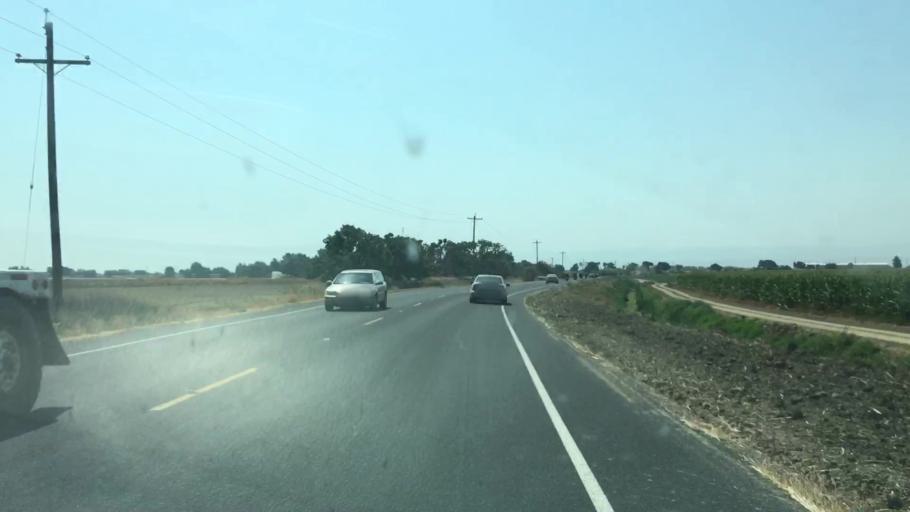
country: US
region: California
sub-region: San Joaquin County
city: Tracy
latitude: 37.8286
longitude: -121.4503
